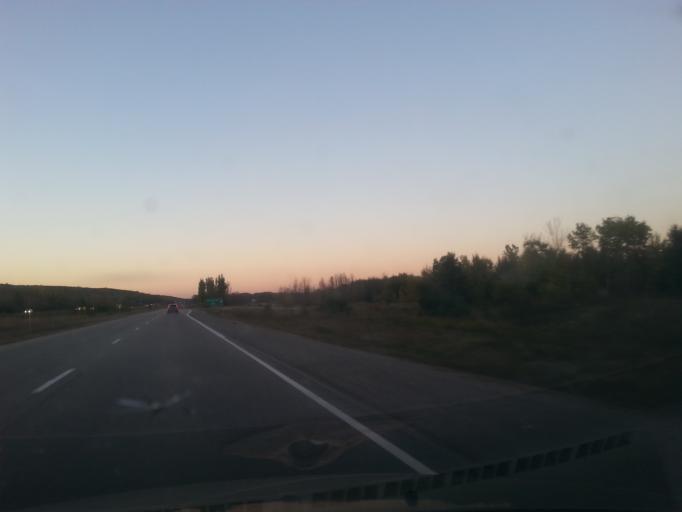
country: CA
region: Ontario
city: Orillia
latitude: 44.6699
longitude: -79.6431
